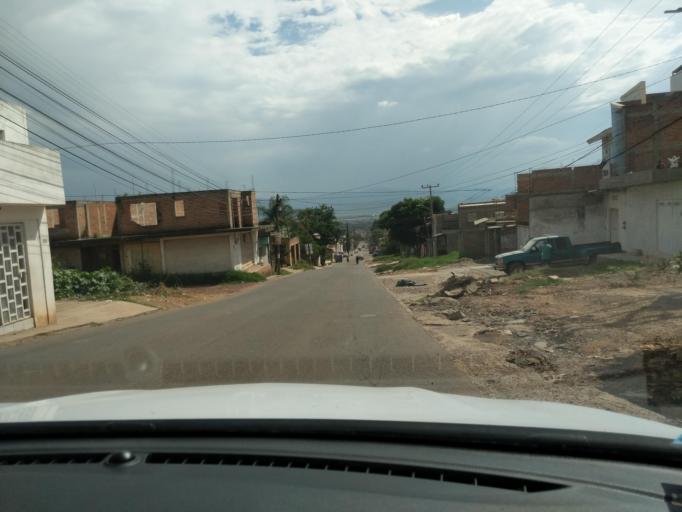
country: MX
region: Jalisco
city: San Jose del Castillo
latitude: 20.5202
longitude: -103.2346
